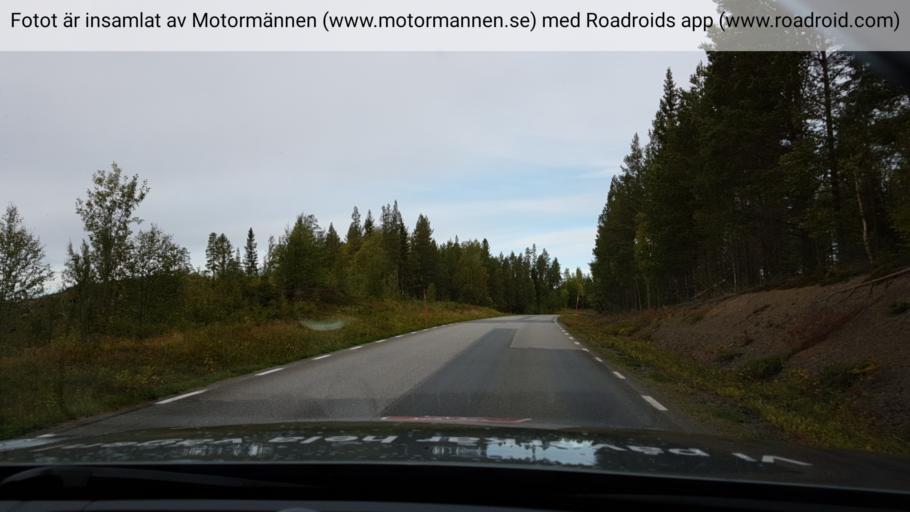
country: SE
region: Jaemtland
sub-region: Krokoms Kommun
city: Krokom
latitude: 63.2827
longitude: 14.2721
